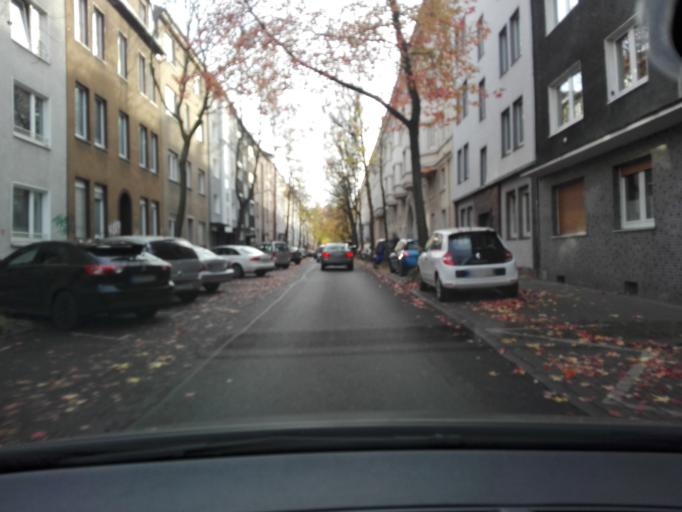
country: DE
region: North Rhine-Westphalia
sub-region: Regierungsbezirk Arnsberg
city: Dortmund
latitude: 51.5110
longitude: 7.4875
